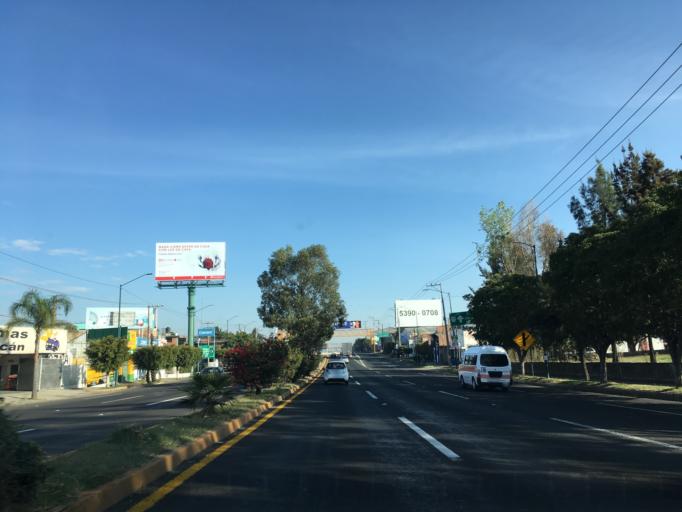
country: MX
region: Michoacan
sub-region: Tarimbaro
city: Fraccionamiento Privadas del Sol
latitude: 19.7282
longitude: -101.1832
